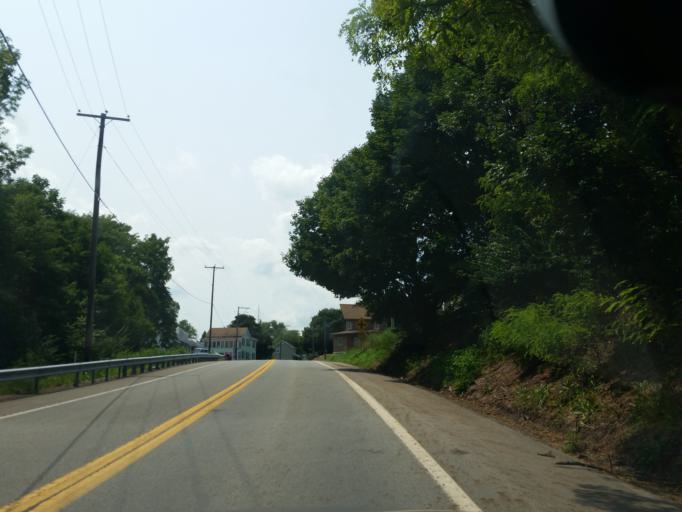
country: US
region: Pennsylvania
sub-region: Dauphin County
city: Elizabethville
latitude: 40.5484
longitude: -76.8791
